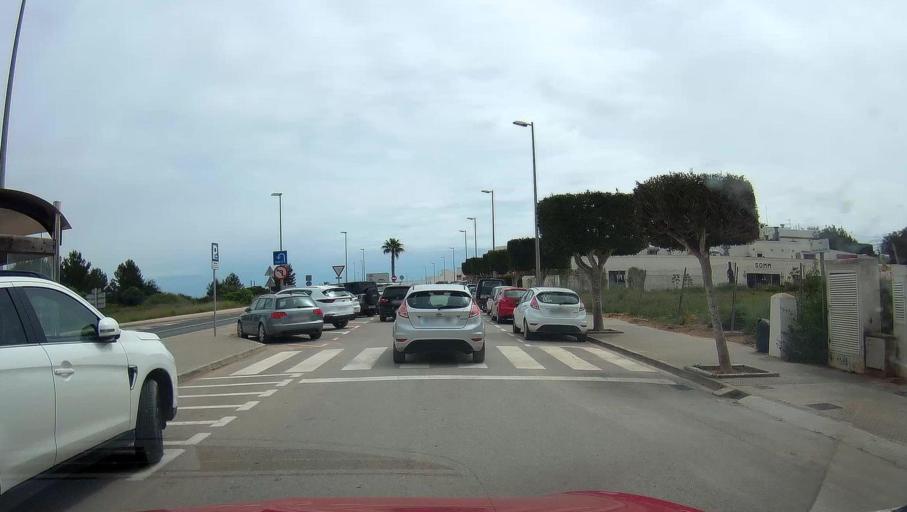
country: ES
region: Balearic Islands
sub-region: Illes Balears
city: Ibiza
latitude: 38.9986
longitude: 1.4302
